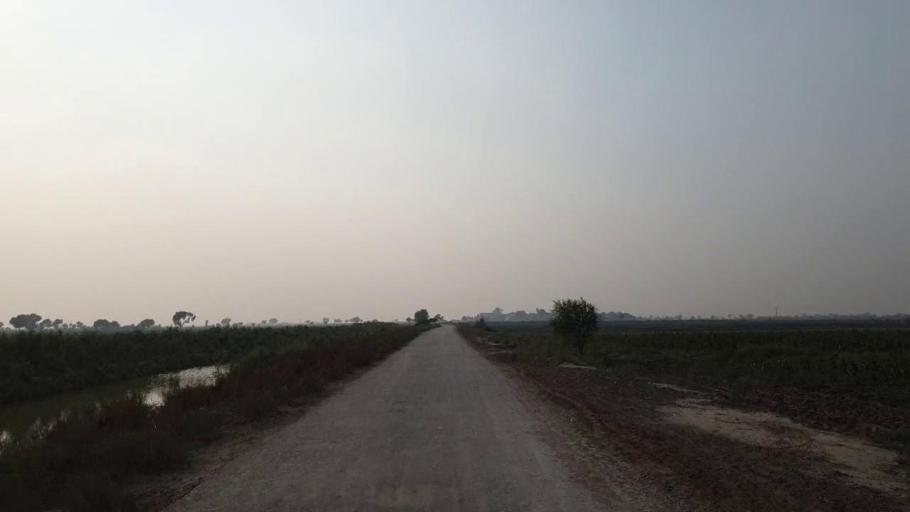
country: PK
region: Sindh
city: Bhan
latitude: 26.4884
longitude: 67.7140
